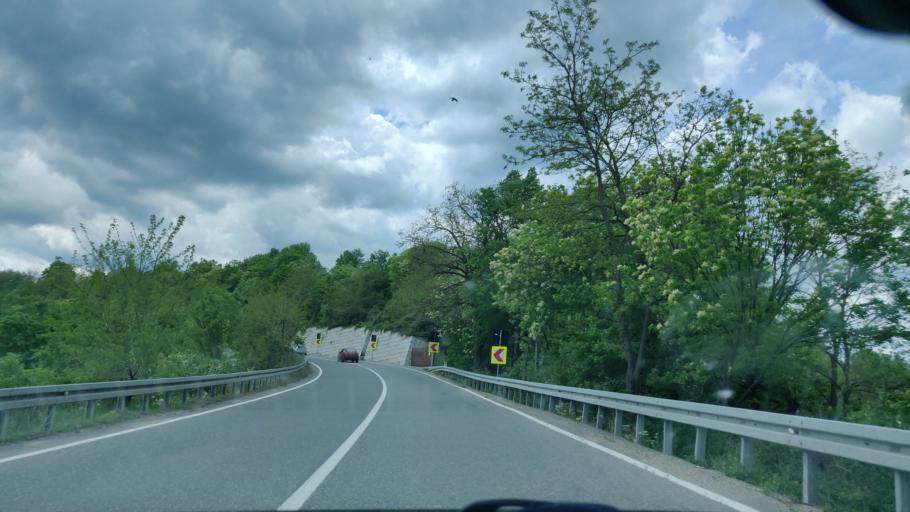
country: RO
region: Vrancea
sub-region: Comuna Negrilesti
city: Negrilesti
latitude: 45.9227
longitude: 26.6973
